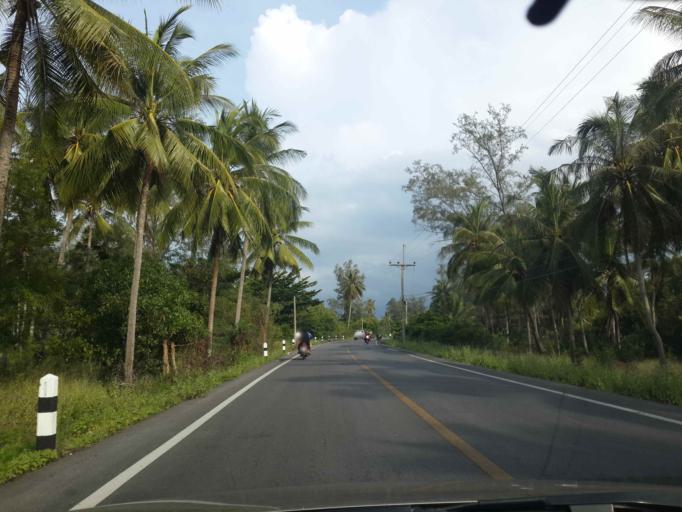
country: TH
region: Pattani
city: Yaring
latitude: 6.9022
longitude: 101.3586
